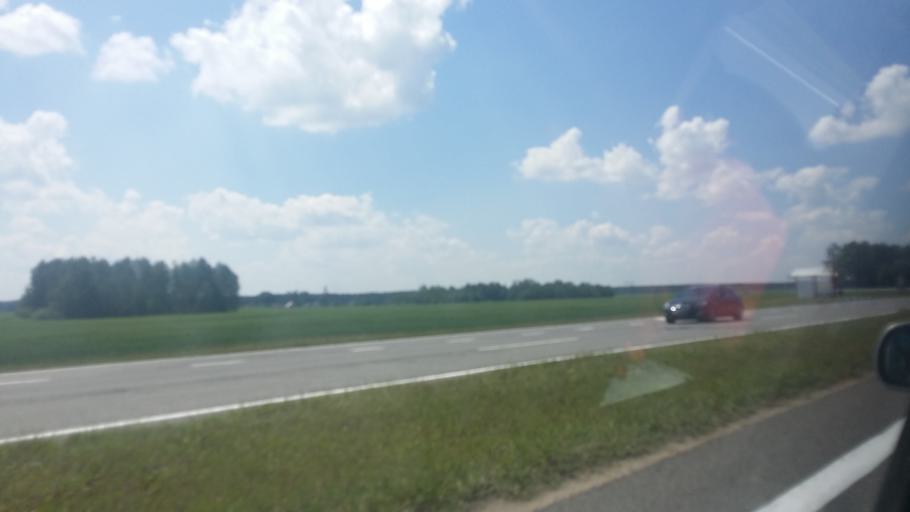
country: BY
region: Minsk
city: Smilavichy
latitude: 53.7642
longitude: 28.1356
